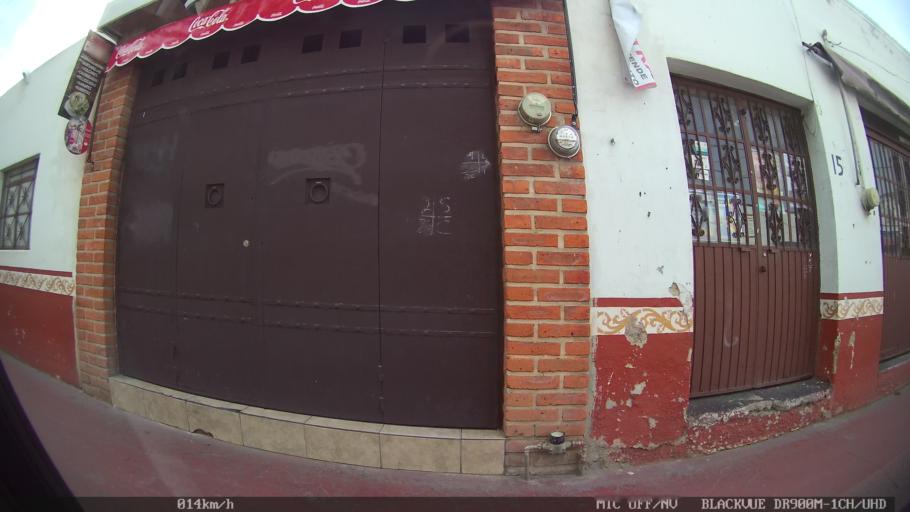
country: MX
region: Jalisco
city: Tonala
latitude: 20.6208
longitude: -103.2434
